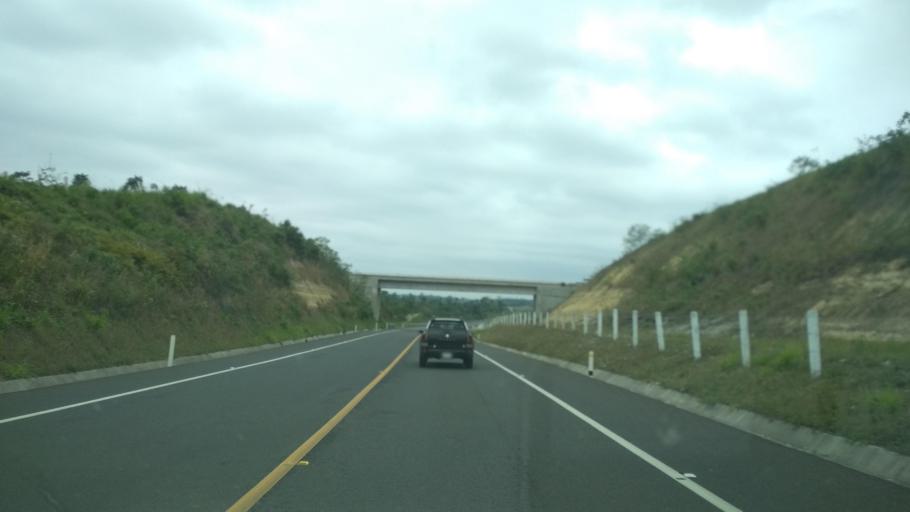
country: MX
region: Veracruz
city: Agua Dulce
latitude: 20.4341
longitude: -97.2305
